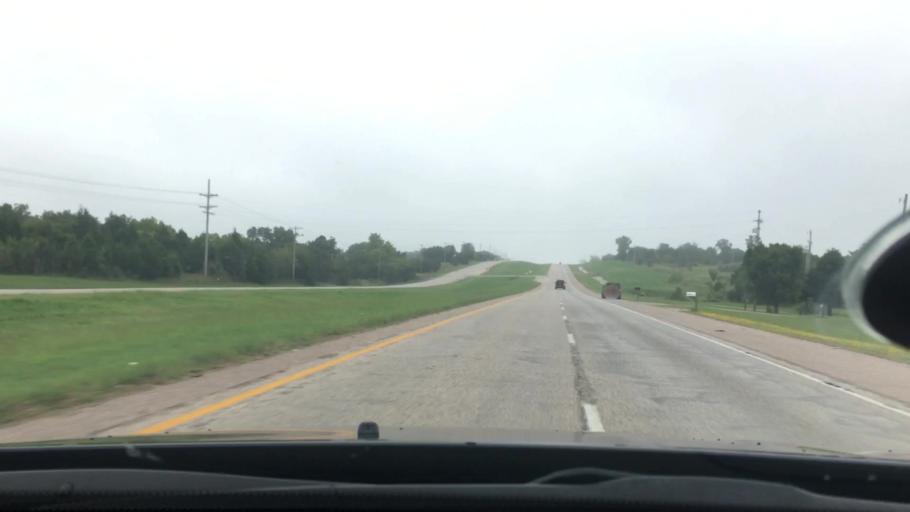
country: US
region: Oklahoma
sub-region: Seminole County
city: Seminole
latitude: 35.2803
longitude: -96.6707
